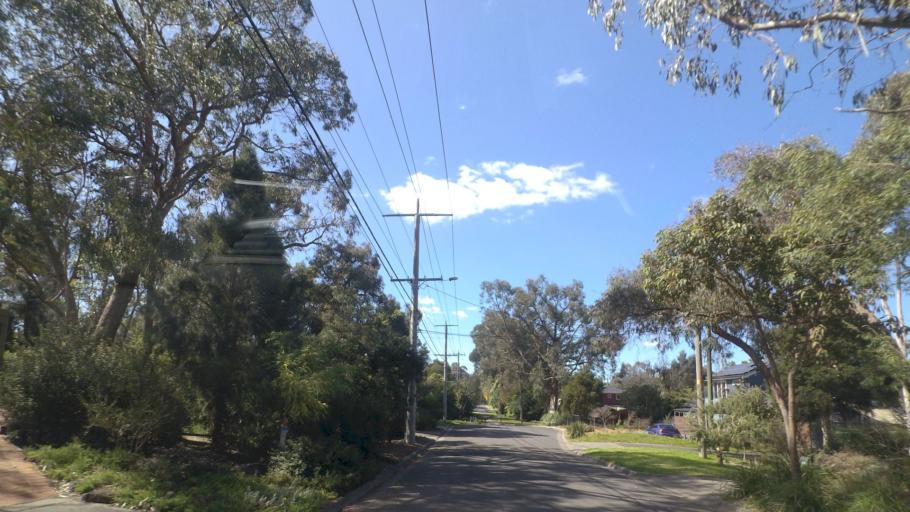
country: AU
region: Victoria
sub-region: Maroondah
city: Heathmont
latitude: -37.8351
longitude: 145.2488
